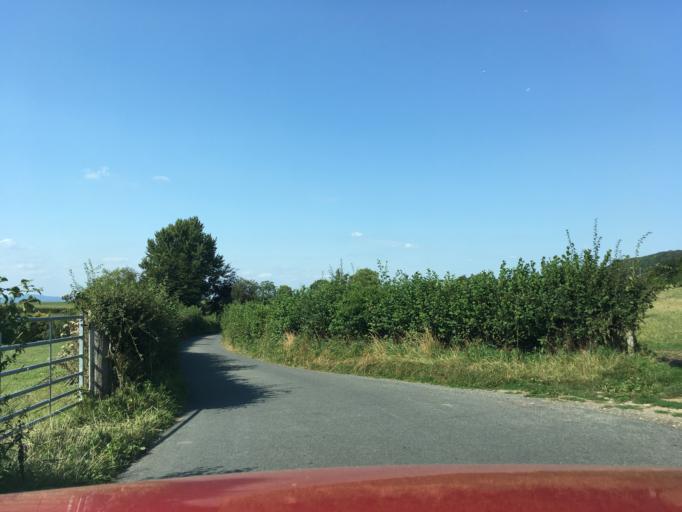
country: GB
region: England
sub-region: Gloucestershire
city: Dursley
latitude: 51.6962
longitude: -2.3160
